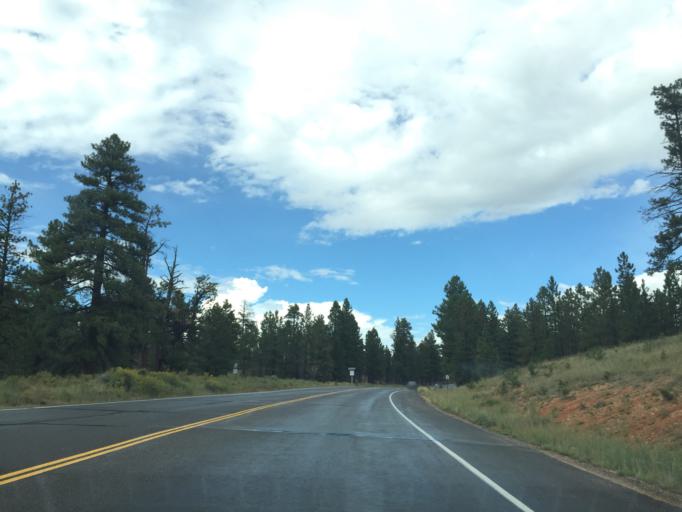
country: US
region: Utah
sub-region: Garfield County
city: Panguitch
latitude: 37.6413
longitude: -112.1685
